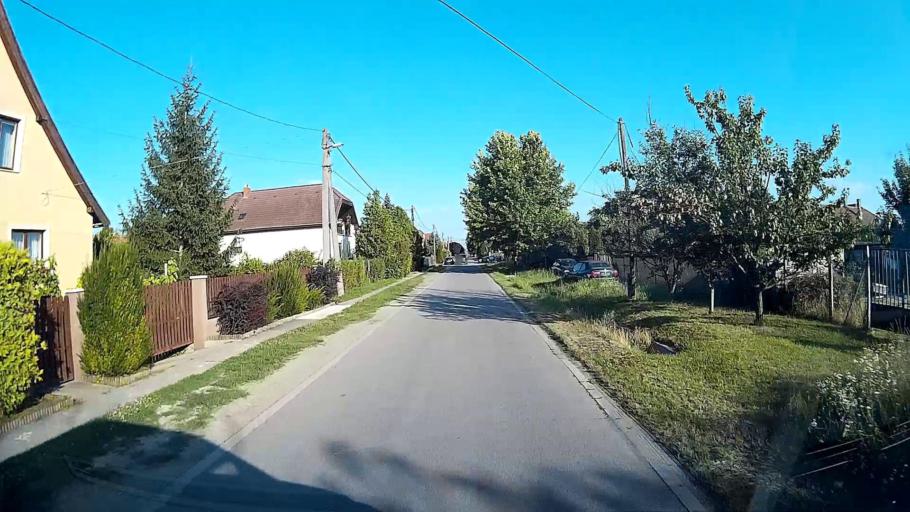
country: HU
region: Pest
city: Tahitotfalu
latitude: 47.7548
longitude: 19.0962
